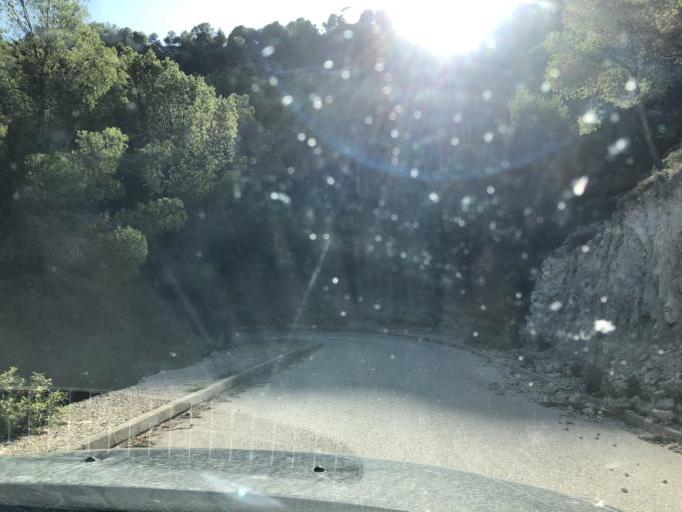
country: ES
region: Balearic Islands
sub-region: Illes Balears
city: Camp de Mar
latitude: 39.5369
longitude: 2.4044
